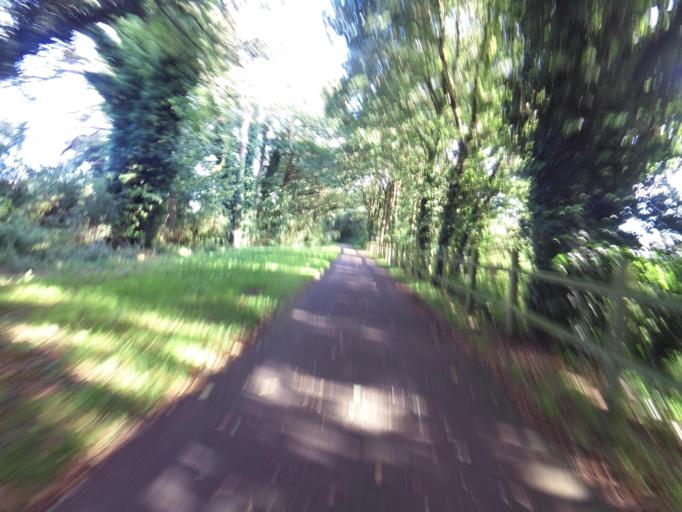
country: FR
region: Brittany
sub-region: Departement du Morbihan
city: Guillac
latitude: 47.8967
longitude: -2.4364
